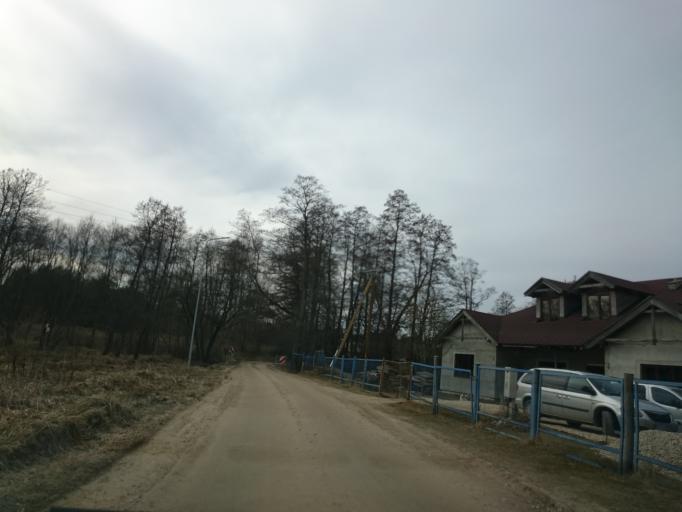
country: LV
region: Garkalne
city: Garkalne
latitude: 57.0165
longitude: 24.3925
